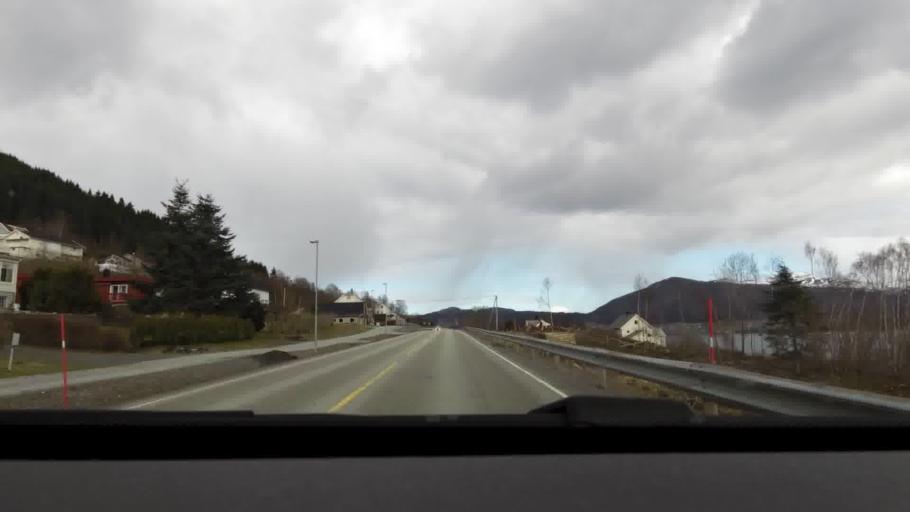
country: NO
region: More og Romsdal
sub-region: Eide
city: Eide
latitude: 62.9246
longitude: 7.4473
